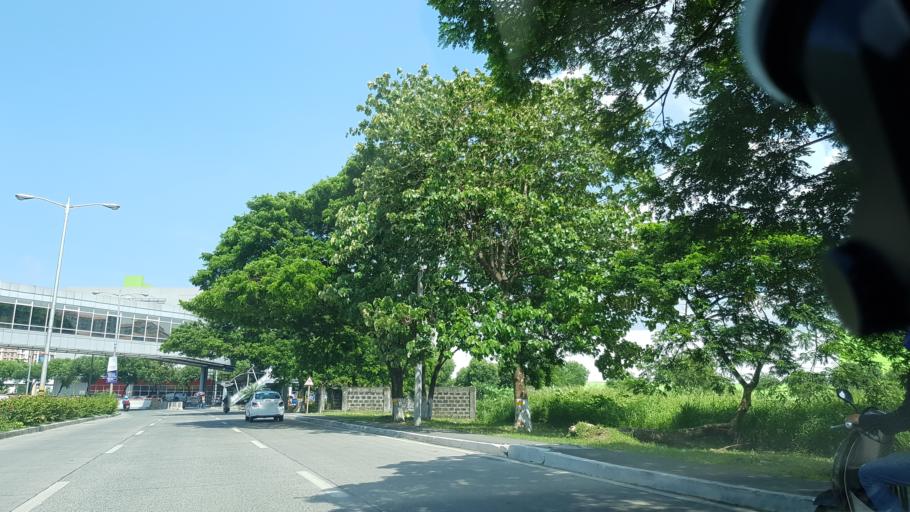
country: PH
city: Sambayanihan People's Village
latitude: 14.4832
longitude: 120.9915
